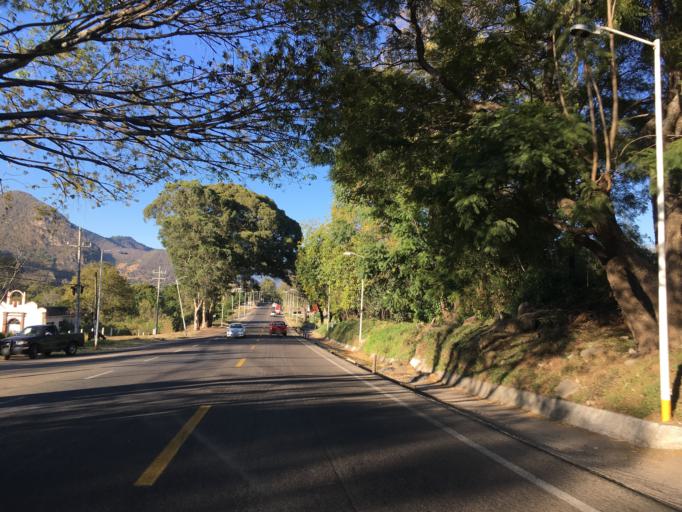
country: MX
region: Michoacan
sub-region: Tuxpan
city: La Soledad
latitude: 19.5425
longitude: -100.4748
